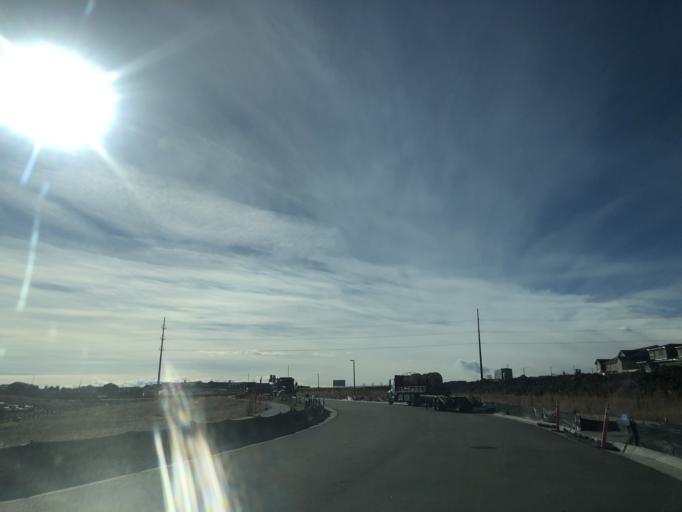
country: US
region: Colorado
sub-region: Douglas County
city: Stonegate
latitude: 39.5543
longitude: -104.8040
